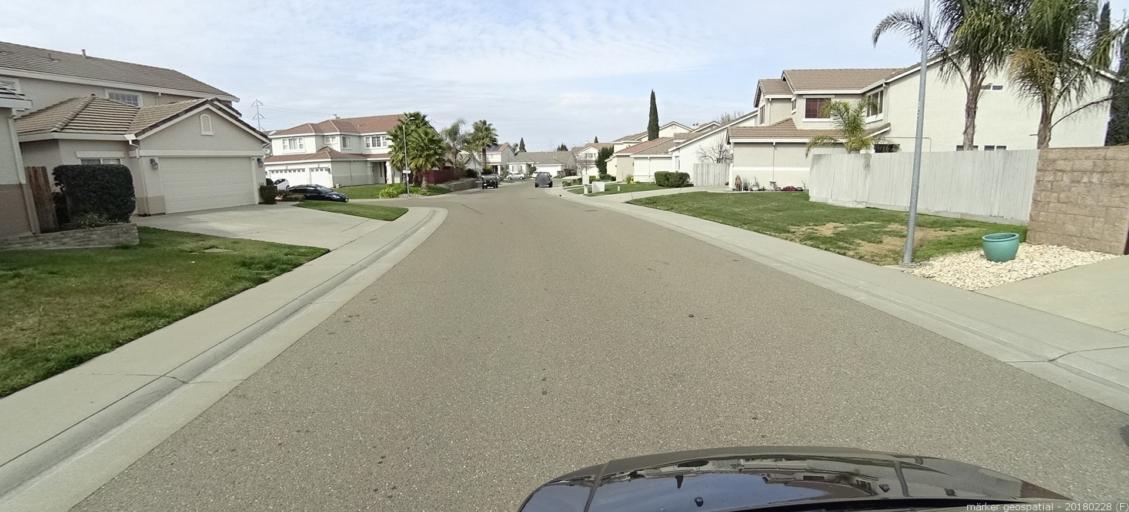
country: US
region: California
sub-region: Sacramento County
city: Antelope
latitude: 38.7116
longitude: -121.3445
